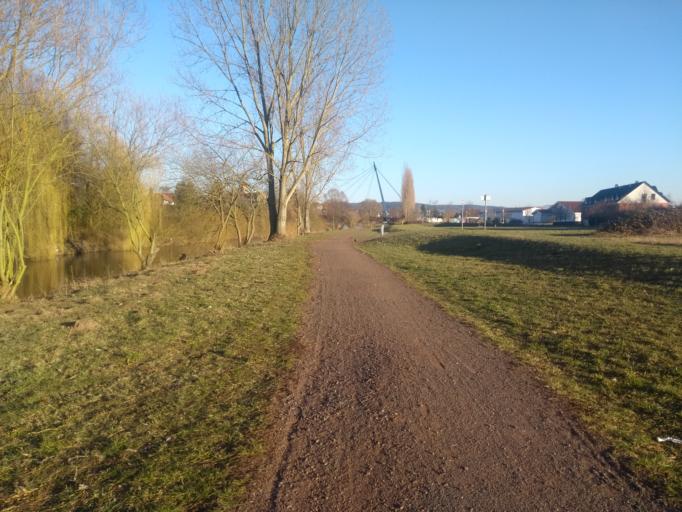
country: DE
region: Thuringia
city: Breitungen
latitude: 50.7604
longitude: 10.3302
